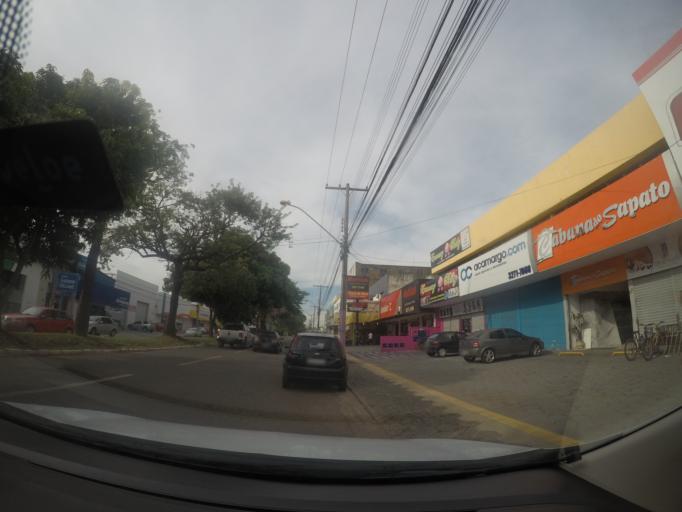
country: BR
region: Goias
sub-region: Goiania
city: Goiania
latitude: -16.6772
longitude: -49.3071
